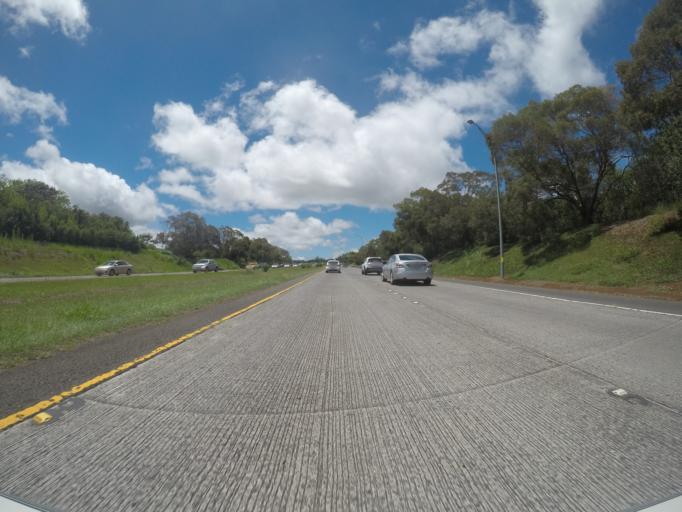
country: US
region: Hawaii
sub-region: Honolulu County
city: Waipi'o Acres
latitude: 21.4820
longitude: -158.0247
